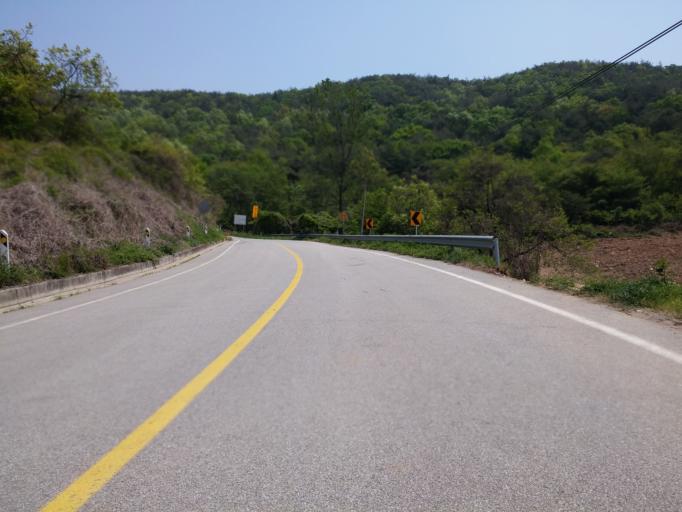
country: KR
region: Chungcheongbuk-do
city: Okcheon
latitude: 36.4213
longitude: 127.5808
